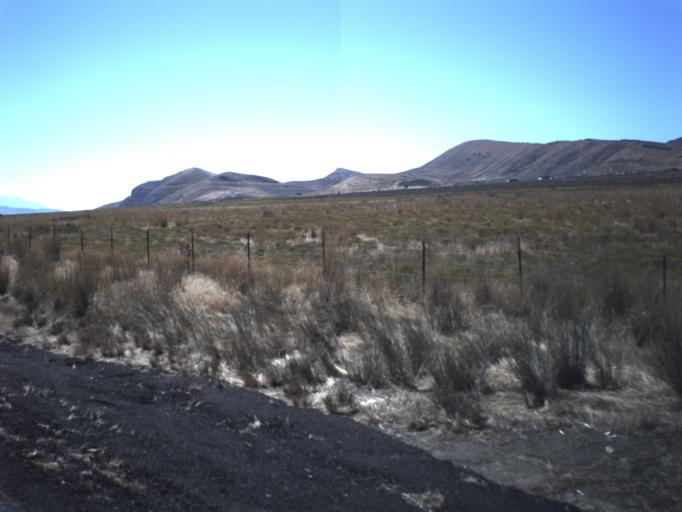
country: US
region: Utah
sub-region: Utah County
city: Saratoga Springs
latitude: 40.2855
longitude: -111.8744
